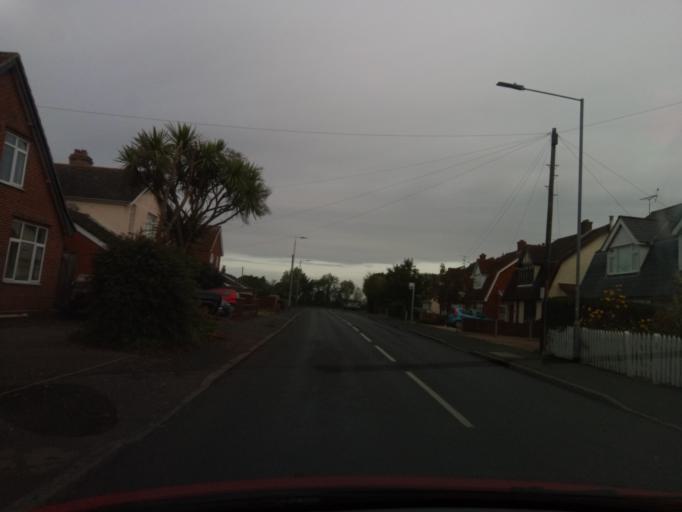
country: GB
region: England
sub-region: Essex
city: West Mersea
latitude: 51.7829
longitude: 0.9198
